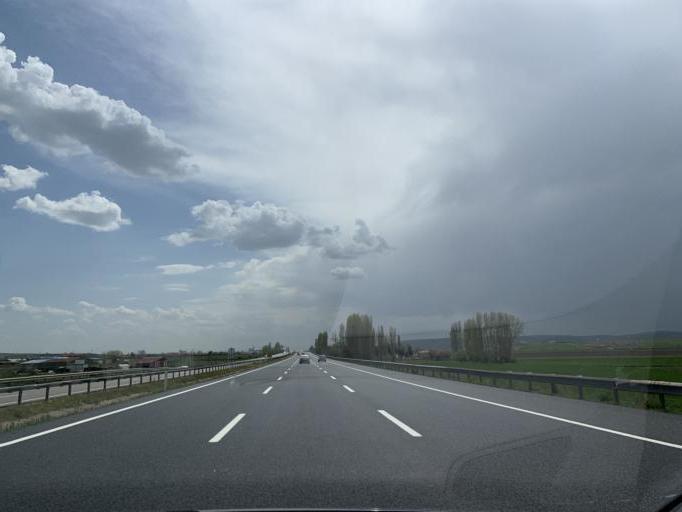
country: TR
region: Ankara
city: Temelli
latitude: 39.6779
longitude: 32.2370
